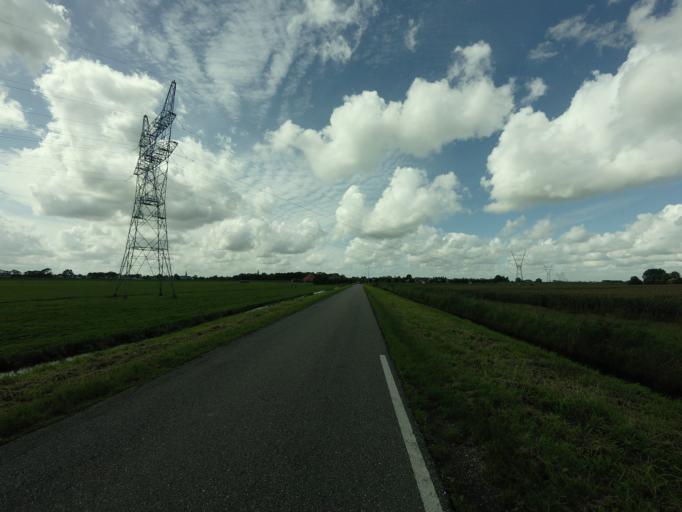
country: NL
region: North Holland
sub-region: Gemeente Purmerend
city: Purmerend
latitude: 52.4640
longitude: 4.9642
